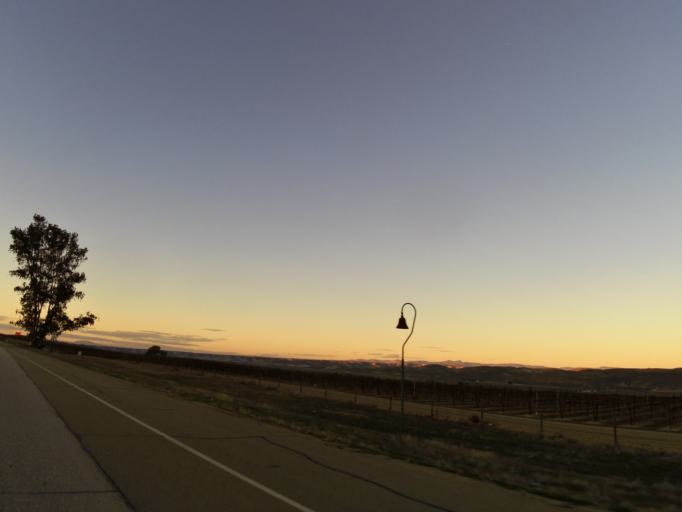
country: US
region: California
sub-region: Monterey County
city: King City
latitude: 36.0168
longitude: -120.9251
